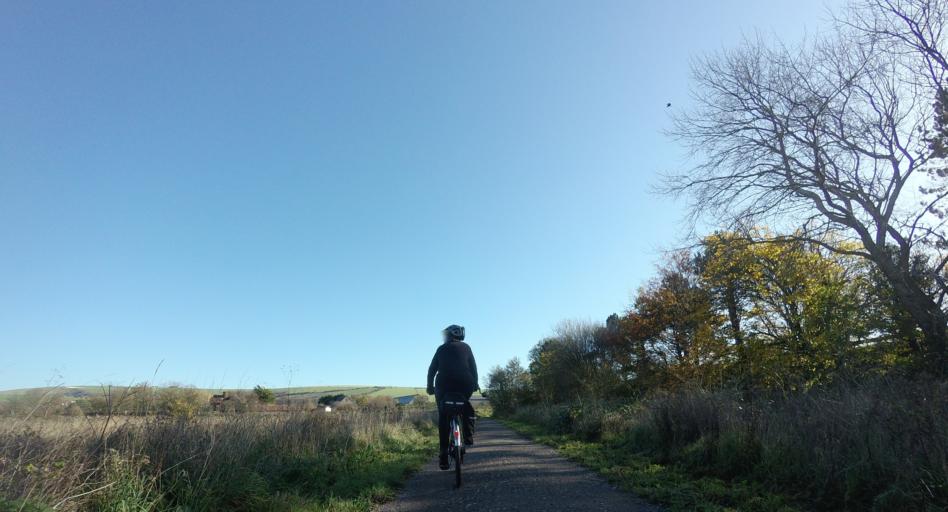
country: GB
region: England
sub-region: West Sussex
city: Steyning
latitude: 50.8783
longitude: -0.3058
